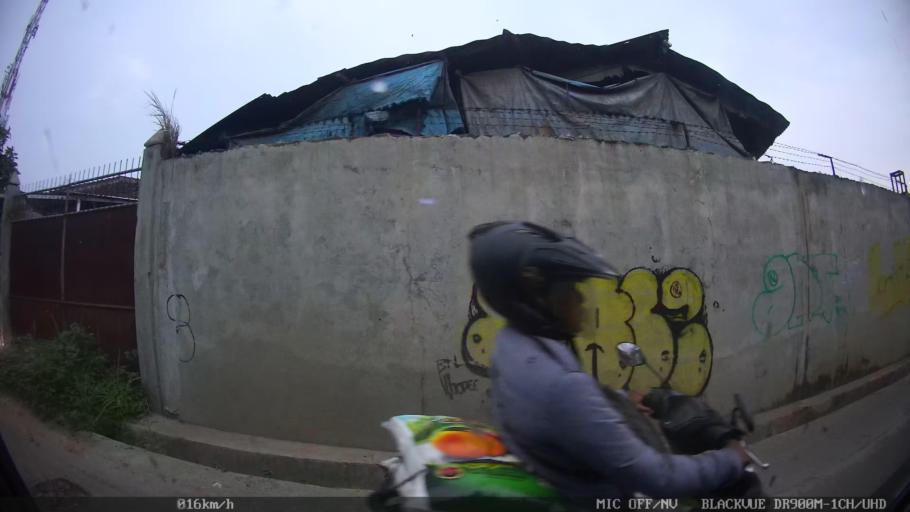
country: ID
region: Lampung
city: Kedaton
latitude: -5.4010
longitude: 105.2757
